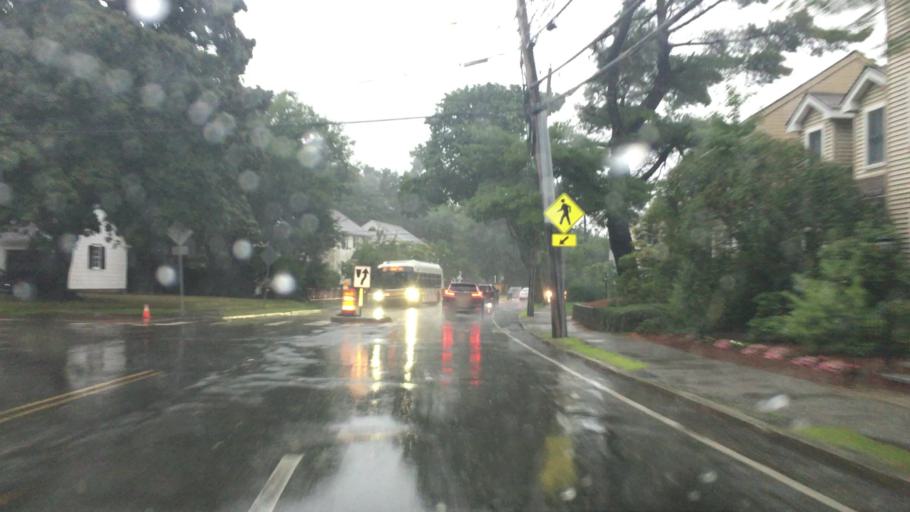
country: US
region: Massachusetts
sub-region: Middlesex County
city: Arlington
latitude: 42.4215
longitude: -71.1623
